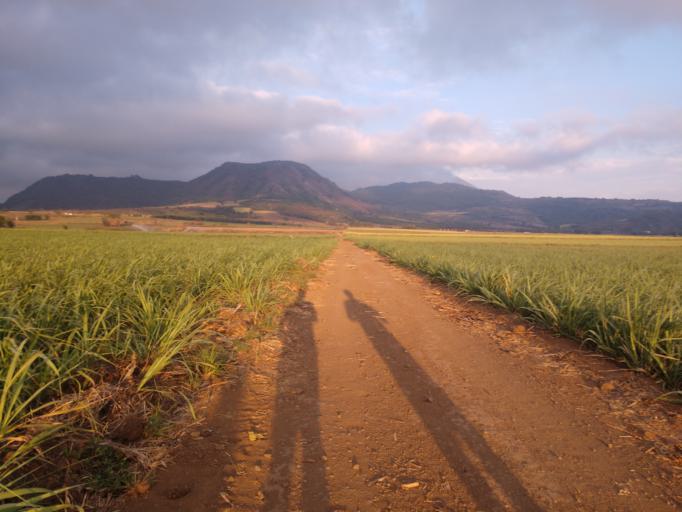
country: MX
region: Nayarit
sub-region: Tepic
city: La Corregidora
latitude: 21.4838
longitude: -104.8056
